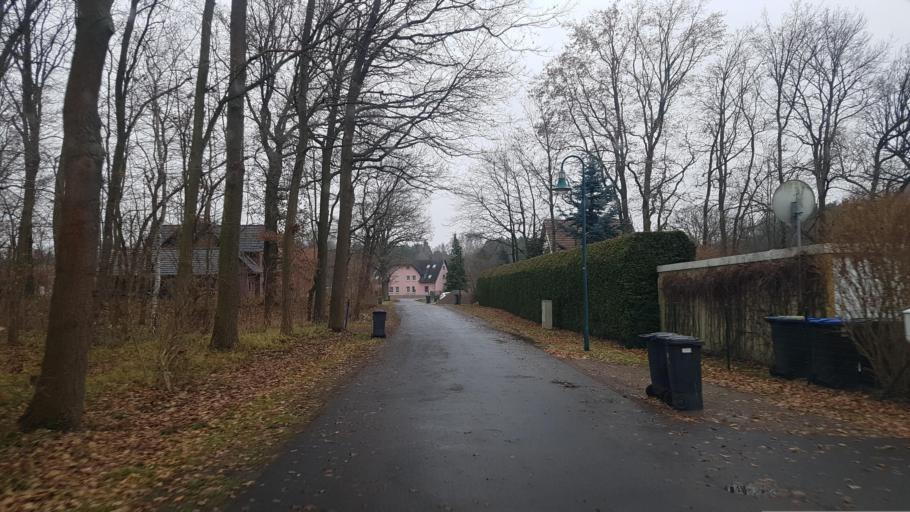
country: DE
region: Brandenburg
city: Cottbus
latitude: 51.6998
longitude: 14.3882
